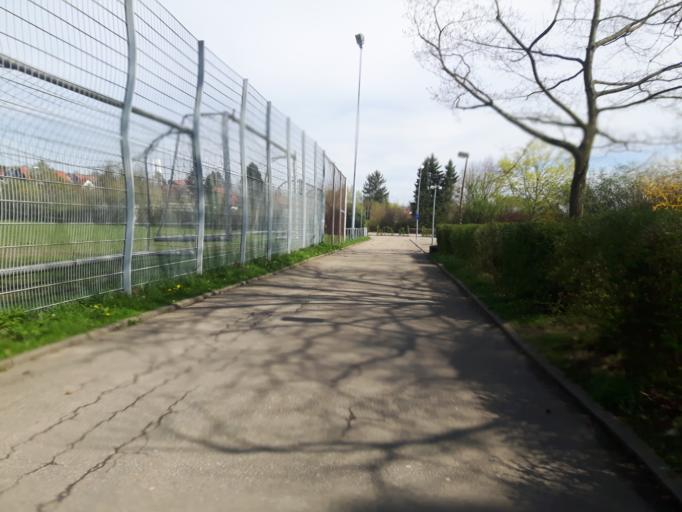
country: DE
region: Baden-Wuerttemberg
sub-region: Regierungsbezirk Stuttgart
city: Schwaigern
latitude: 49.1434
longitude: 9.0481
